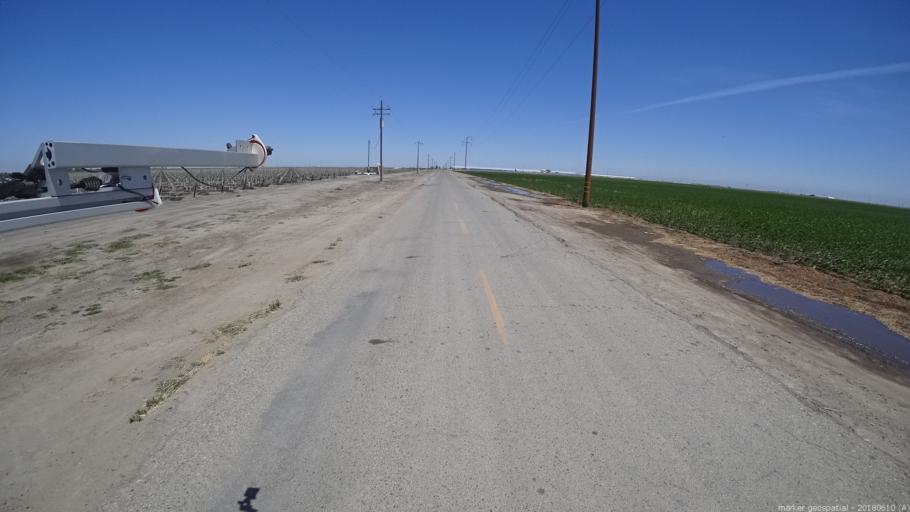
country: US
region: California
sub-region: Merced County
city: Dos Palos
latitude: 37.0504
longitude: -120.5287
